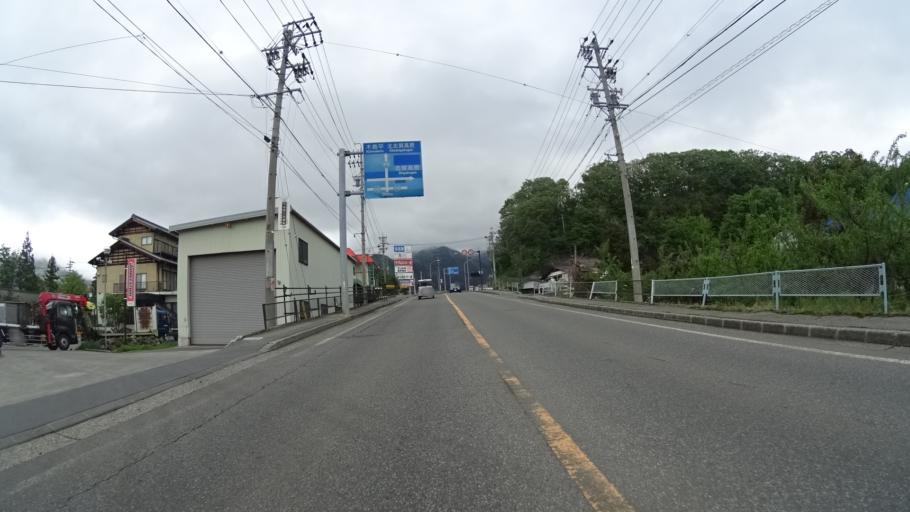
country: JP
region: Nagano
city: Nakano
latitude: 36.7590
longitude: 138.3949
